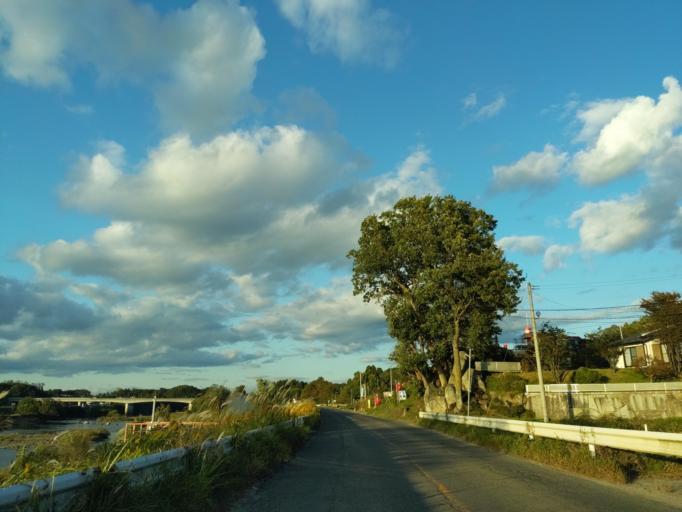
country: JP
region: Fukushima
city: Koriyama
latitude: 37.4359
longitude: 140.4220
